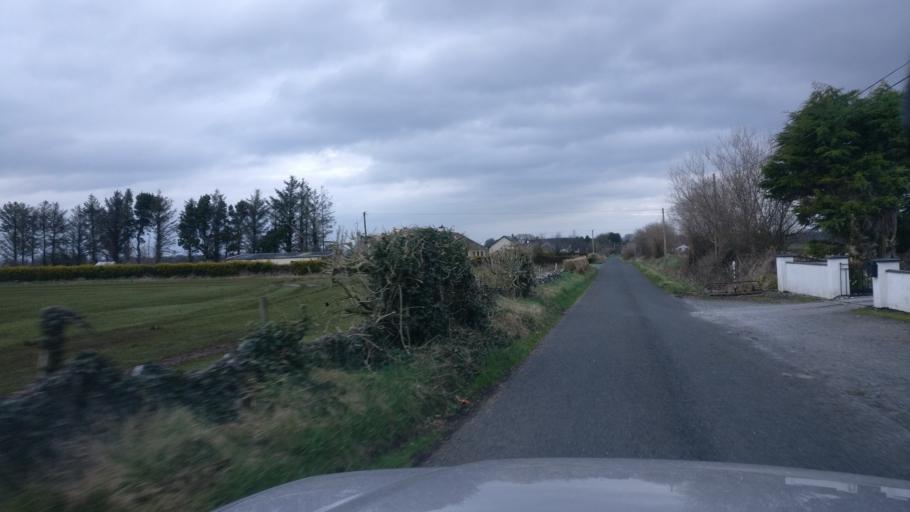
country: IE
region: Connaught
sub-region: County Galway
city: Loughrea
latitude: 53.2549
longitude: -8.5102
